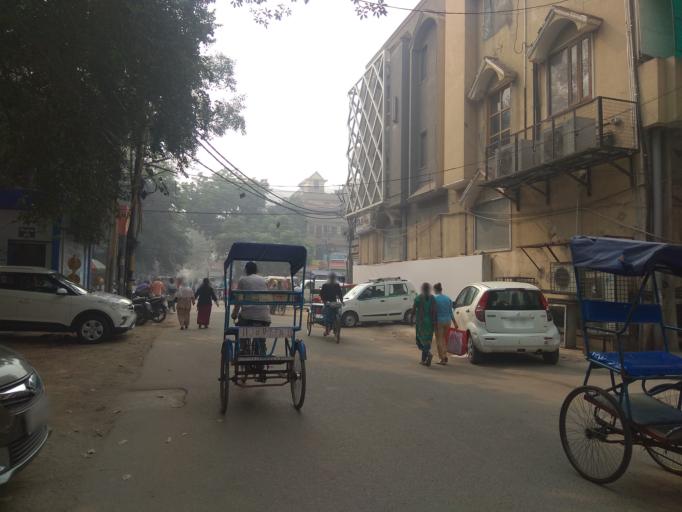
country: IN
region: NCT
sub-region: New Delhi
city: New Delhi
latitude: 28.5694
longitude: 77.2442
